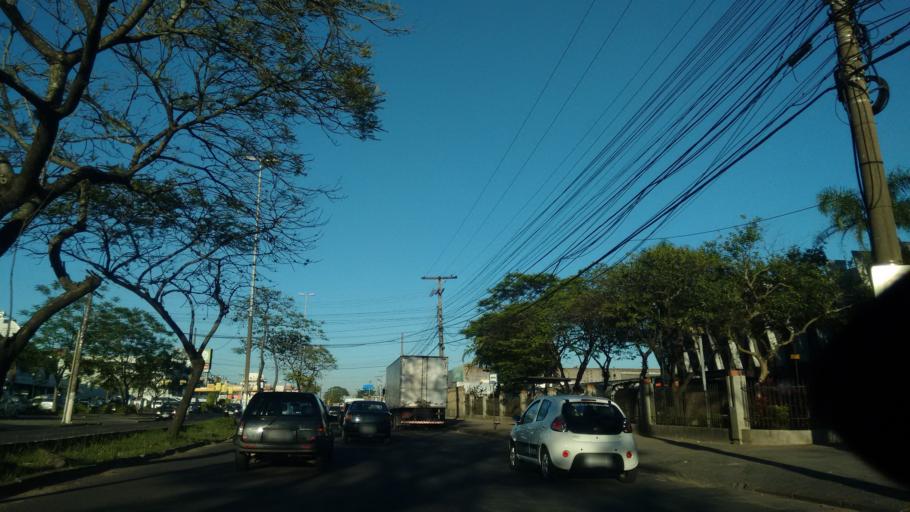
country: BR
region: Rio Grande do Sul
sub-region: Cachoeirinha
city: Cachoeirinha
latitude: -29.9979
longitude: -51.1436
